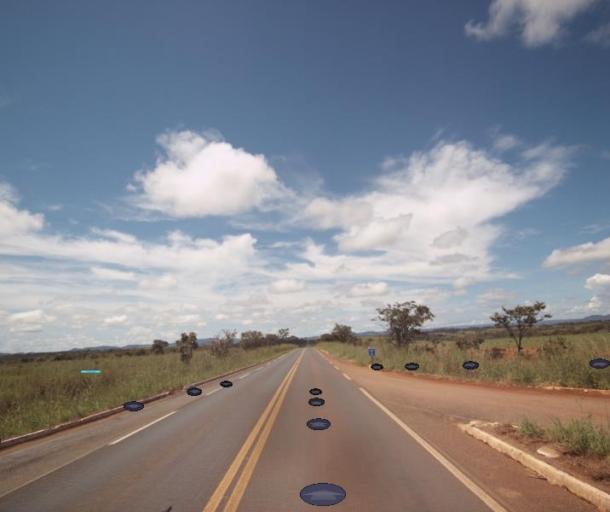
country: BR
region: Goias
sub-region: Padre Bernardo
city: Padre Bernardo
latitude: -15.2913
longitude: -48.2447
